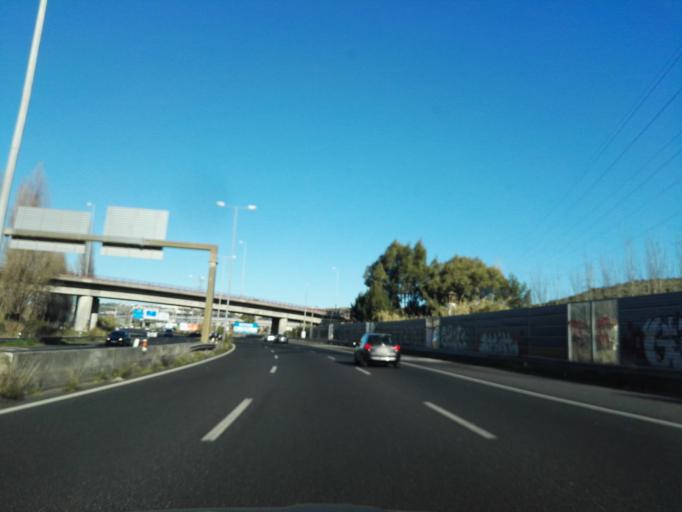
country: PT
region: Lisbon
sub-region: Odivelas
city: Odivelas
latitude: 38.7839
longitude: -9.1782
